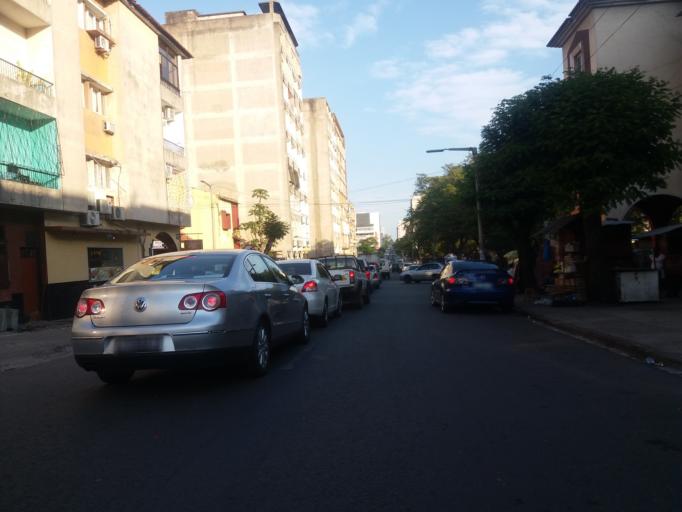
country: MZ
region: Maputo City
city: Maputo
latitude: -25.9612
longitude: 32.5679
